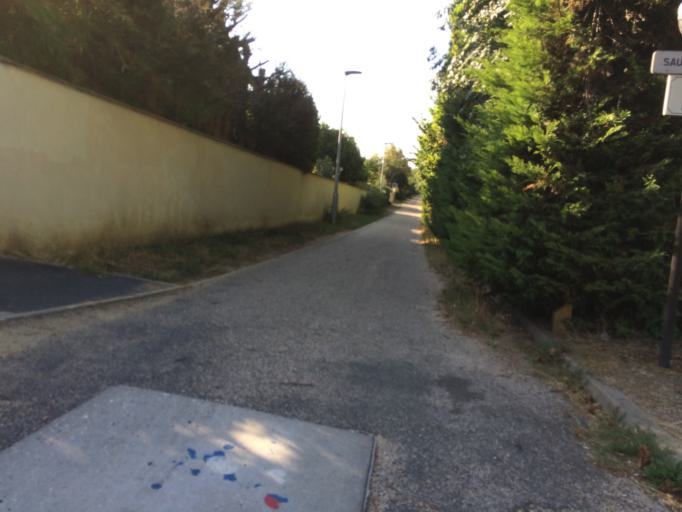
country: FR
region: Ile-de-France
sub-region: Departement de l'Essonne
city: Villemoisson-sur-Orge
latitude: 48.6789
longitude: 2.3265
